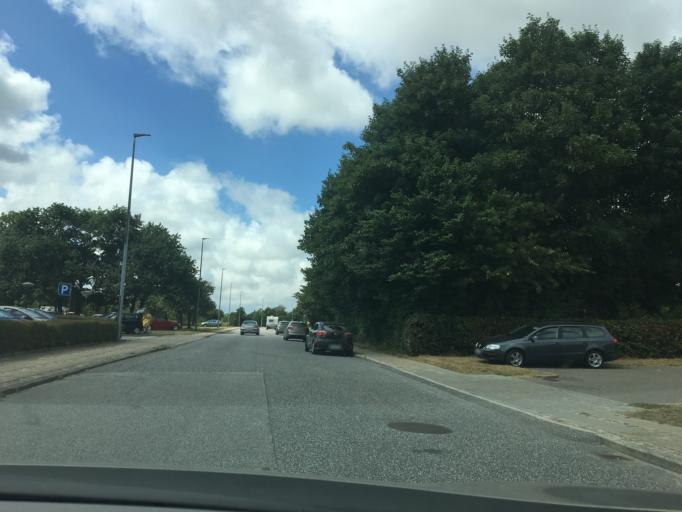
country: DK
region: Central Jutland
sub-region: Ringkobing-Skjern Kommune
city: Tarm
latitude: 55.9081
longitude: 8.5168
